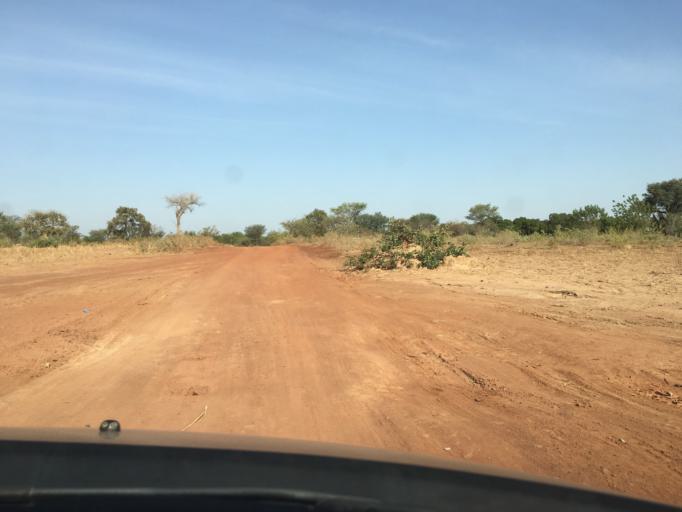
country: BF
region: Plateau-Central
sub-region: Province du Kourweogo
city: Bousse
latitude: 12.5671
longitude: -1.9129
